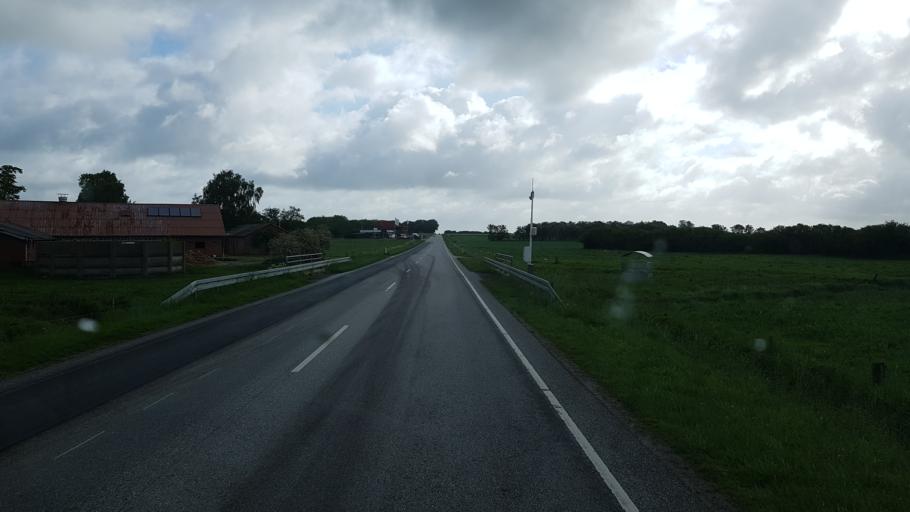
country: DK
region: South Denmark
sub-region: Vejen Kommune
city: Rodding
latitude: 55.3943
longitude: 9.0968
